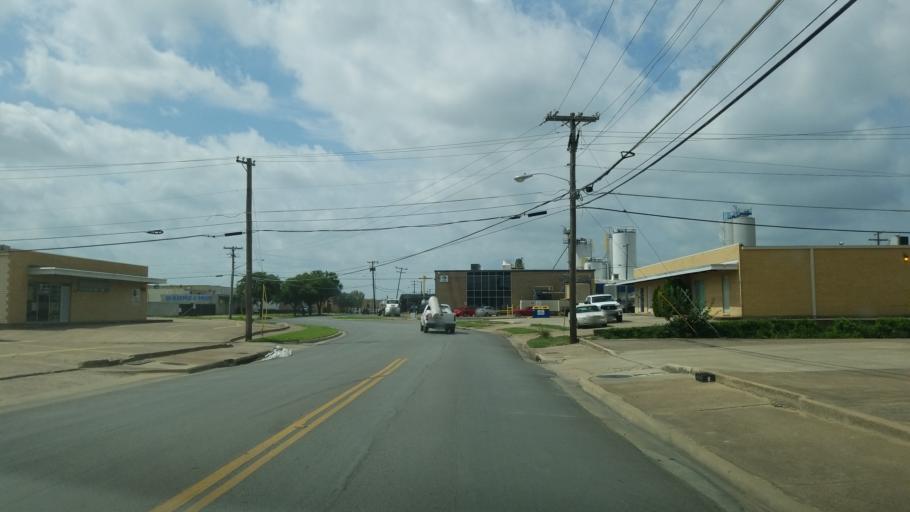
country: US
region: Texas
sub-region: Dallas County
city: Farmers Branch
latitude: 32.8801
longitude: -96.8783
